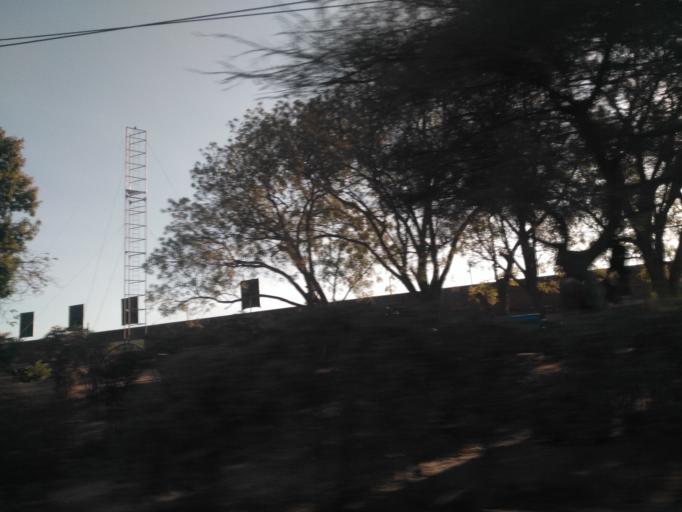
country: TZ
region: Dodoma
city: Dodoma
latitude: -6.1726
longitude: 35.7448
